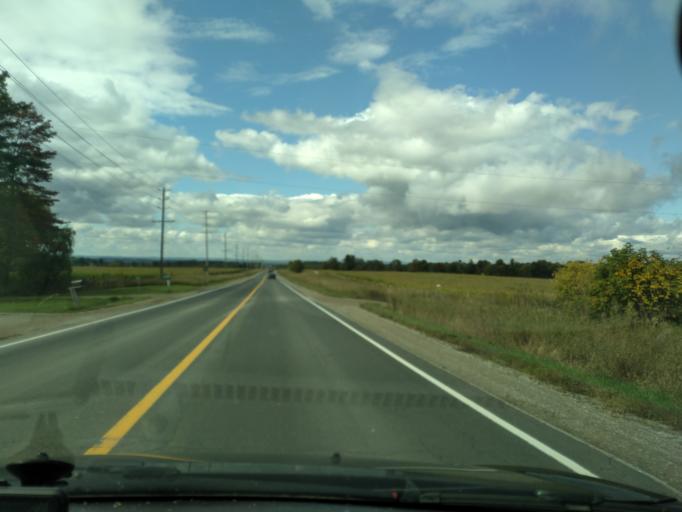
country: CA
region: Ontario
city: Innisfil
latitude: 44.2676
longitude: -79.7359
